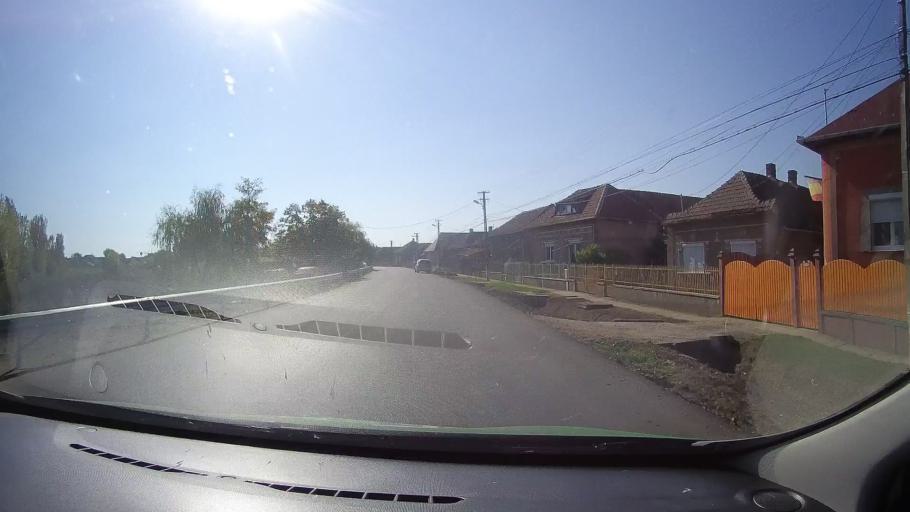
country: RO
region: Satu Mare
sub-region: Comuna Berveni
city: Lucaceni
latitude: 47.7363
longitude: 22.4755
